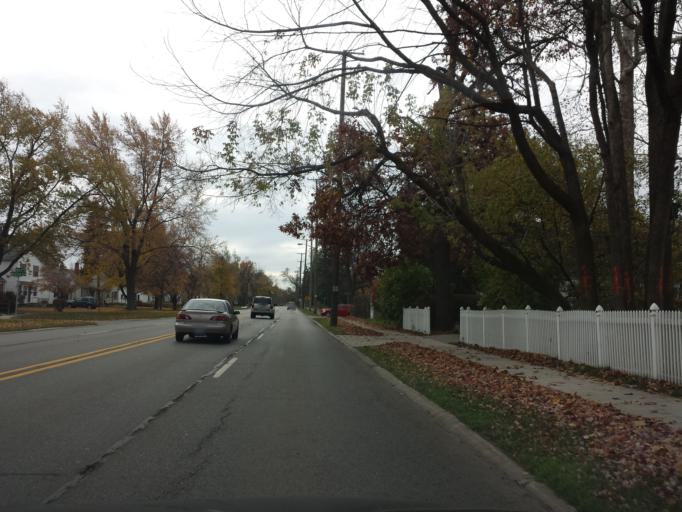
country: US
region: Michigan
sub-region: Oakland County
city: Clawson
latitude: 42.5158
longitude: -83.1455
